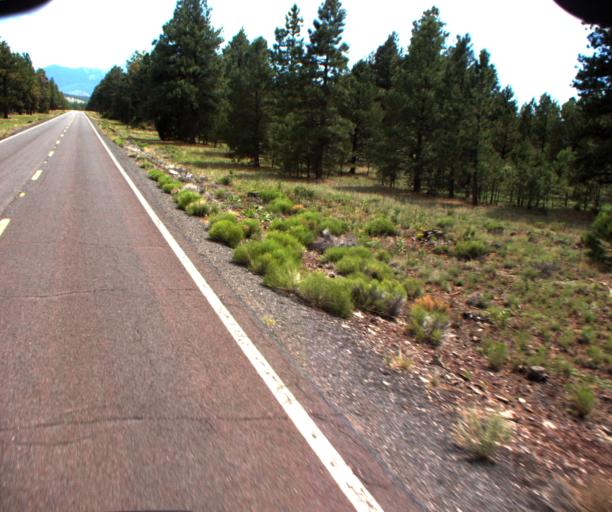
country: US
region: Arizona
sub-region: Coconino County
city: Parks
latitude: 35.4680
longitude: -111.7868
